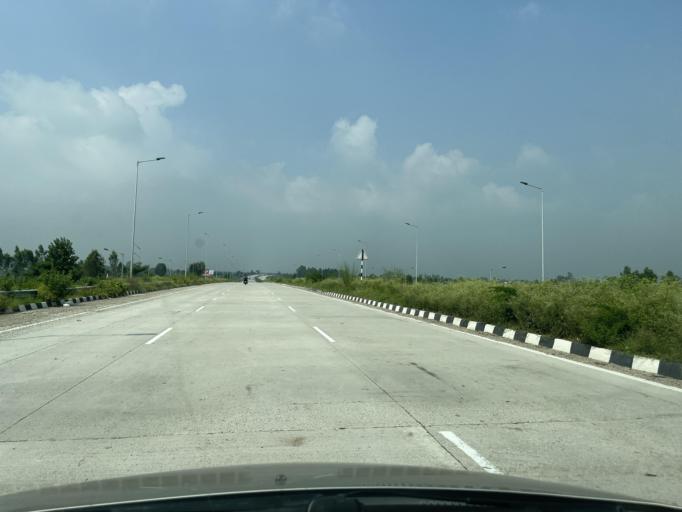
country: IN
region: Uttarakhand
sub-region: Udham Singh Nagar
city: Kashipur
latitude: 29.1654
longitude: 78.9749
